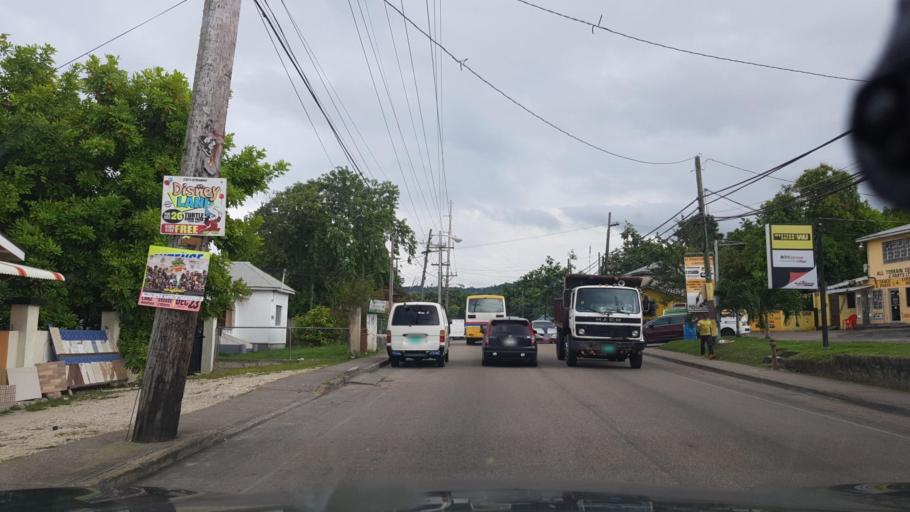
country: JM
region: Saint Ann
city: Saint Ann's Bay
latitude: 18.4453
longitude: -77.2225
